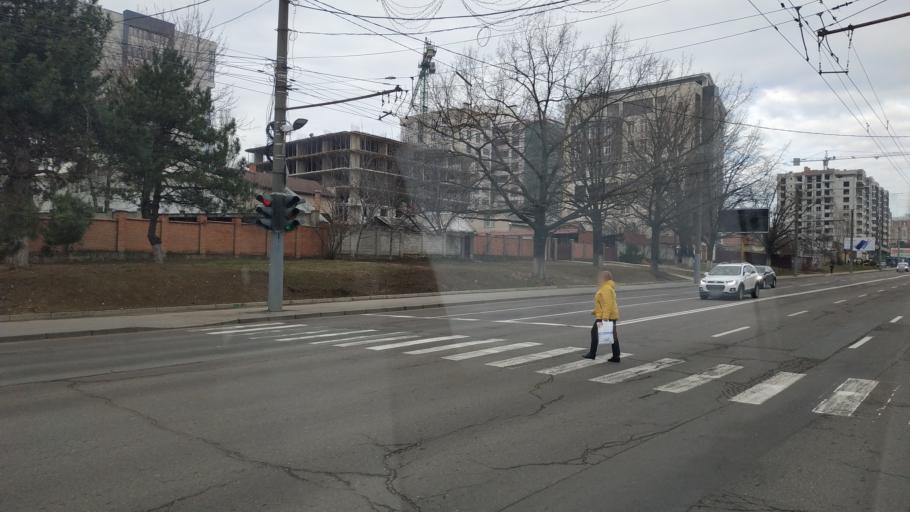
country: MD
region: Chisinau
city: Vatra
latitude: 47.0324
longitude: 28.7822
